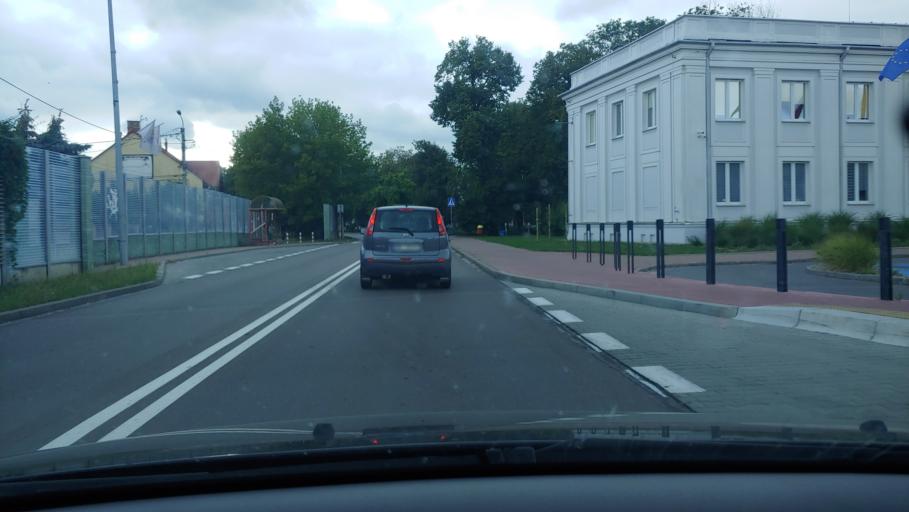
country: PL
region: Subcarpathian Voivodeship
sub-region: Powiat mielecki
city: Mielec
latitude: 50.2890
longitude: 21.4194
